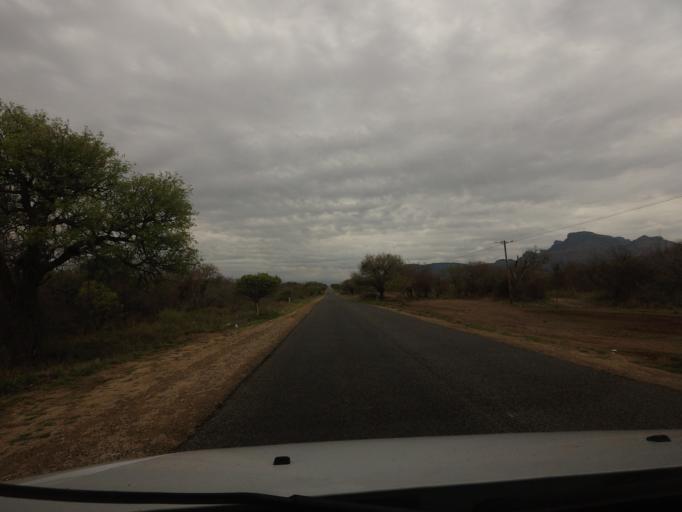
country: ZA
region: Limpopo
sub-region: Mopani District Municipality
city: Hoedspruit
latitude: -24.4719
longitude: 30.8787
